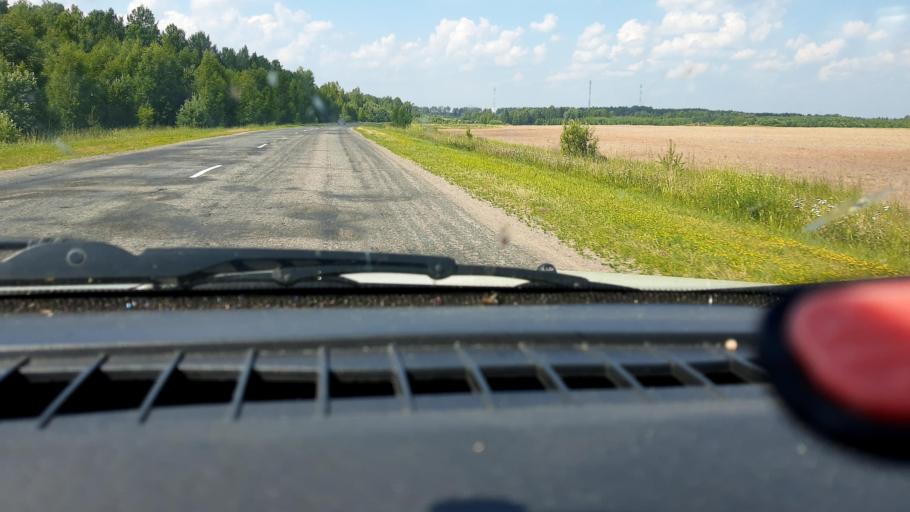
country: RU
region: Nizjnij Novgorod
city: Tonkino
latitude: 57.3578
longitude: 46.4274
